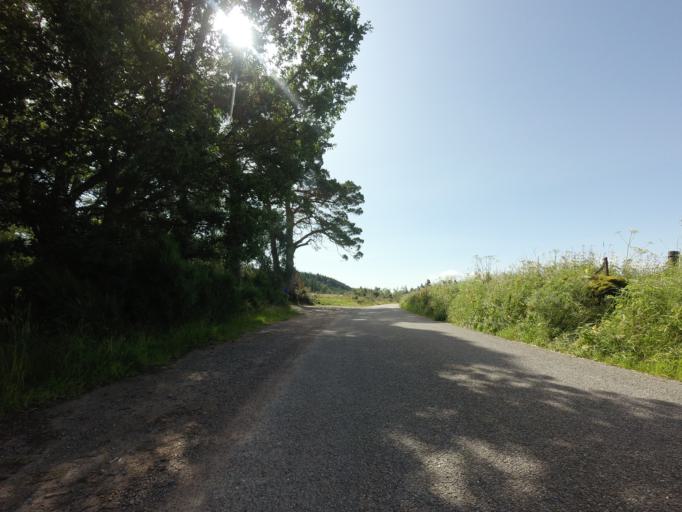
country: GB
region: Scotland
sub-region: Highland
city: Nairn
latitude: 57.5306
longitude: -3.8621
